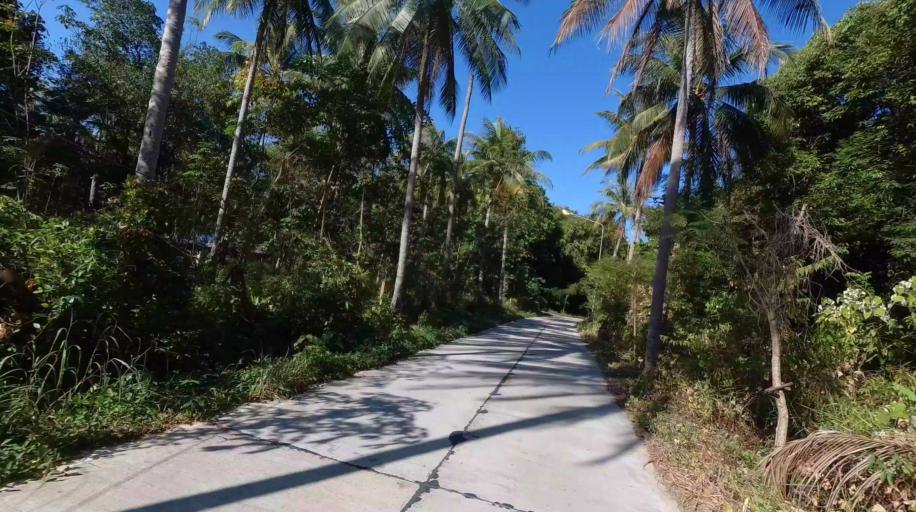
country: TH
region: Trat
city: Ko Kut
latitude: 11.6156
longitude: 102.5412
